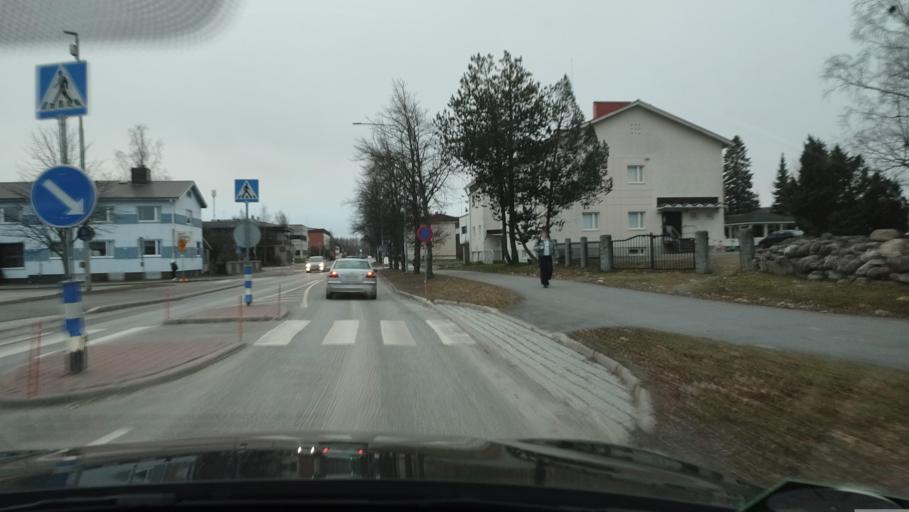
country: FI
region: Southern Ostrobothnia
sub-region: Suupohja
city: Kauhajoki
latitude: 62.4255
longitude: 22.1767
